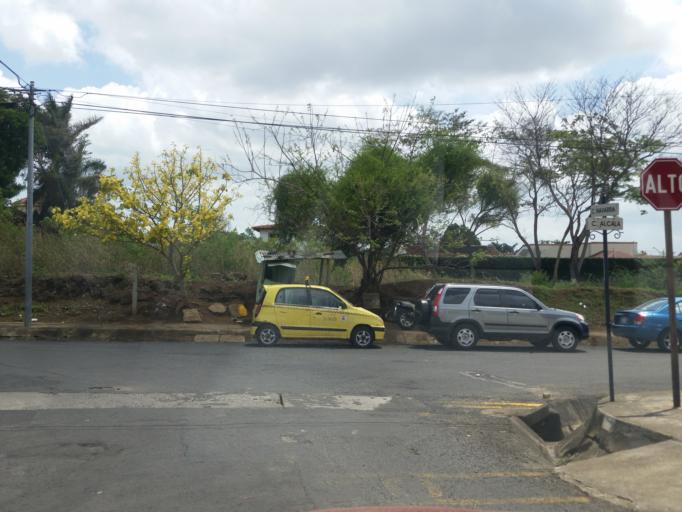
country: NI
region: Managua
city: Managua
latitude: 12.0756
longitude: -86.2376
